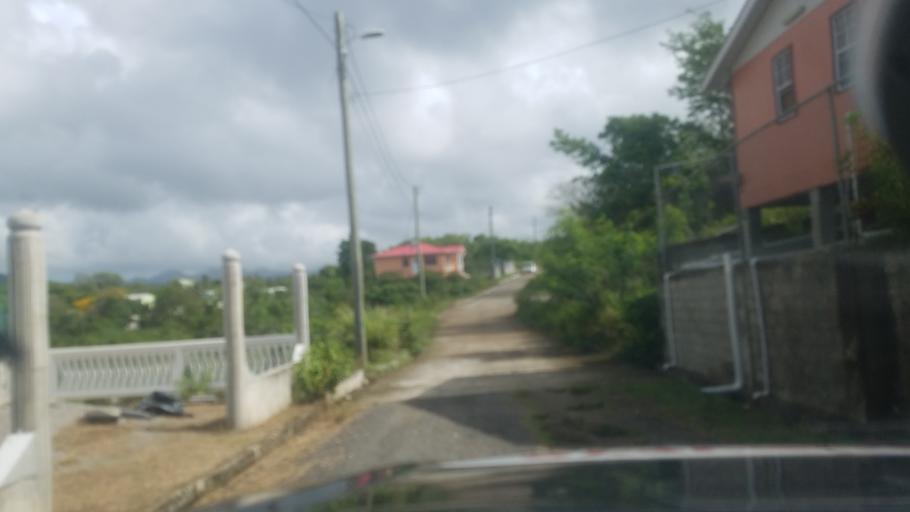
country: LC
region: Laborie Quarter
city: Laborie
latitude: 13.7497
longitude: -60.9770
